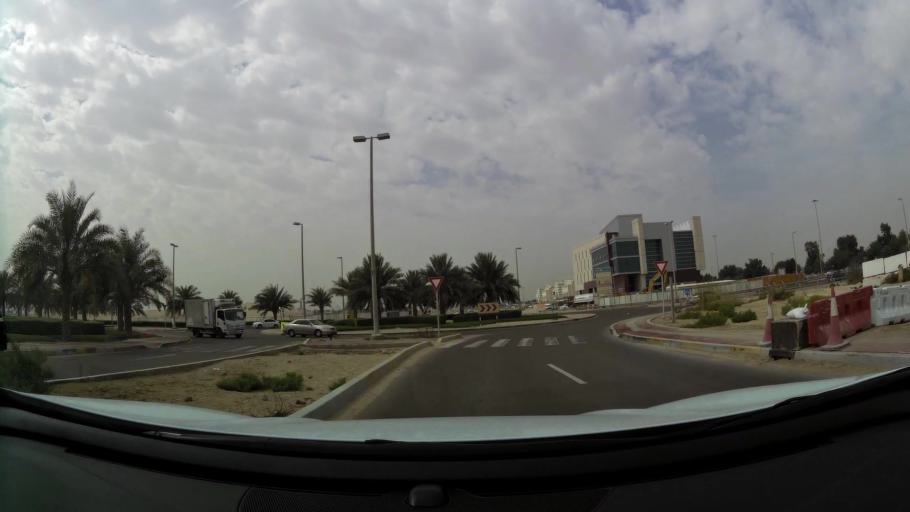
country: AE
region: Abu Dhabi
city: Abu Dhabi
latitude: 24.3192
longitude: 54.6131
